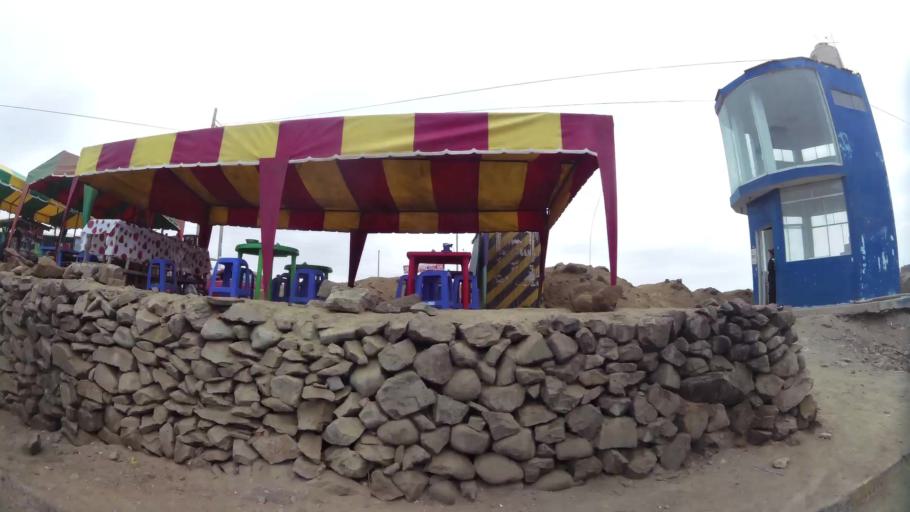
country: PE
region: Lima
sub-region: Lima
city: Pucusana
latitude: -12.4653
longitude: -76.7526
